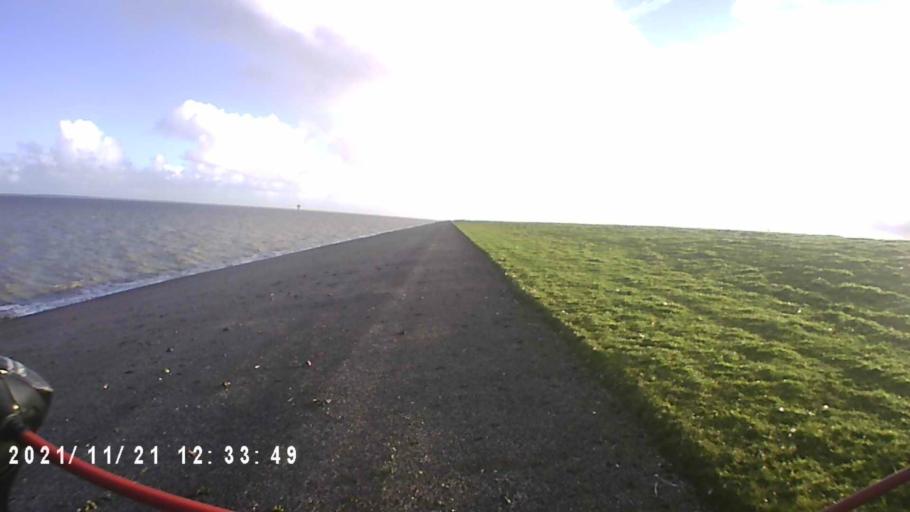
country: NL
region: Friesland
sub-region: Gemeente Dongeradeel
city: Anjum
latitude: 53.4054
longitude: 6.0547
